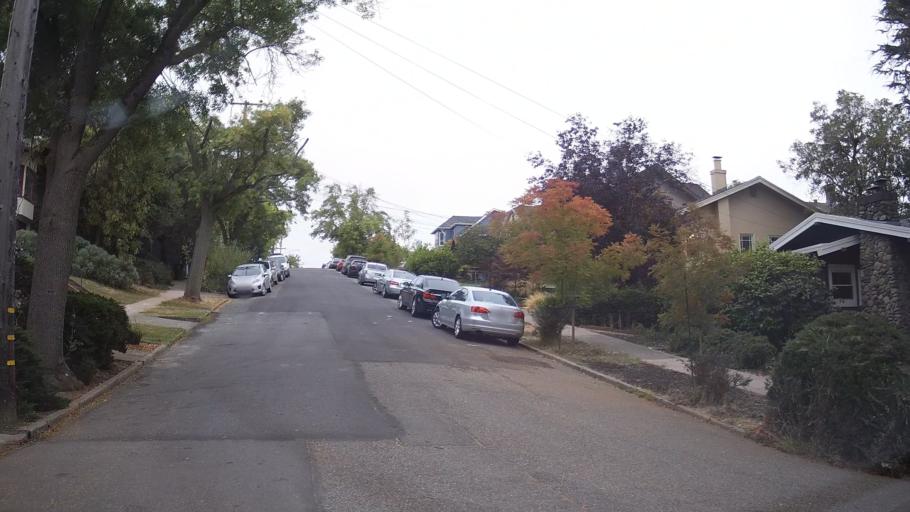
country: US
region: California
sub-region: Alameda County
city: Albany
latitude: 37.8888
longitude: -122.2806
